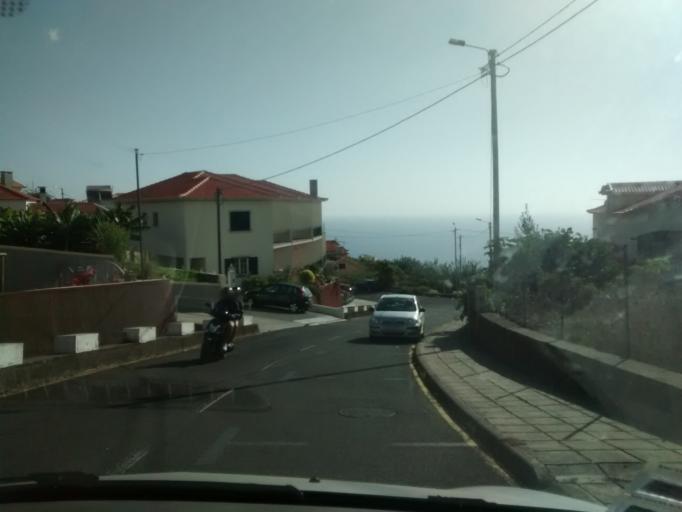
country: PT
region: Madeira
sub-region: Calheta
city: Estreito da Calheta
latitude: 32.7302
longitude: -17.1762
